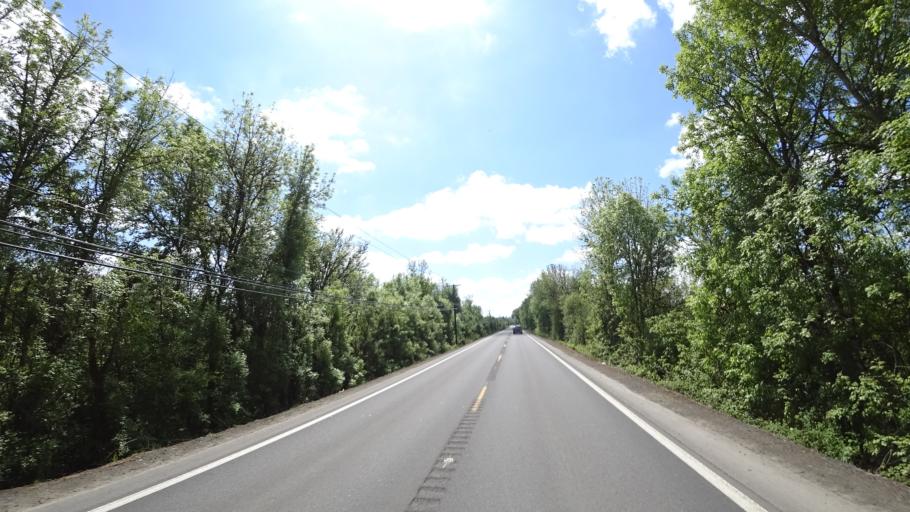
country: US
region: Oregon
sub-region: Washington County
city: Hillsboro
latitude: 45.5075
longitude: -122.9910
